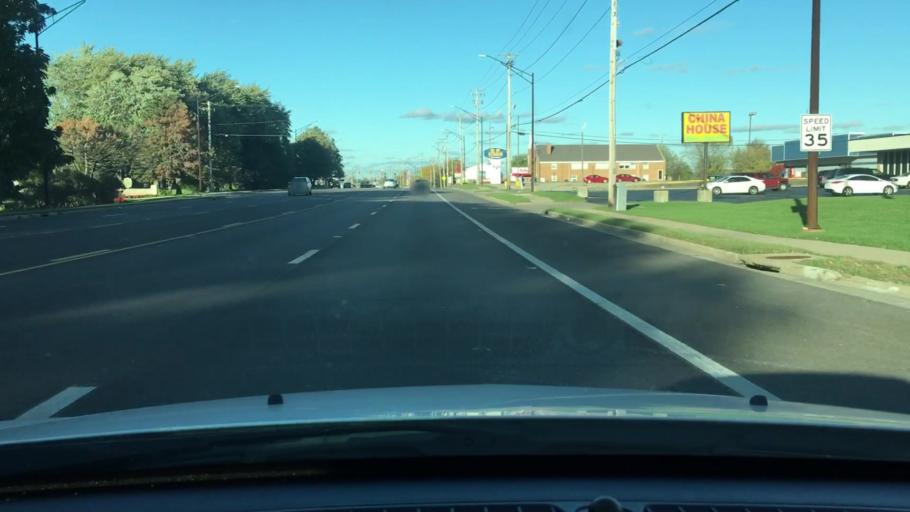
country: US
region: Illinois
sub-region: DeKalb County
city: DeKalb
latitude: 41.9473
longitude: -88.7318
